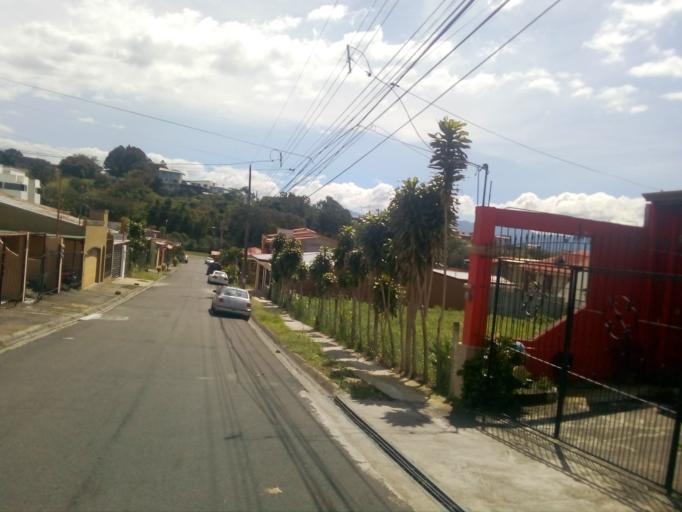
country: CR
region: Alajuela
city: Alajuela
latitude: 10.0186
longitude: -84.1997
